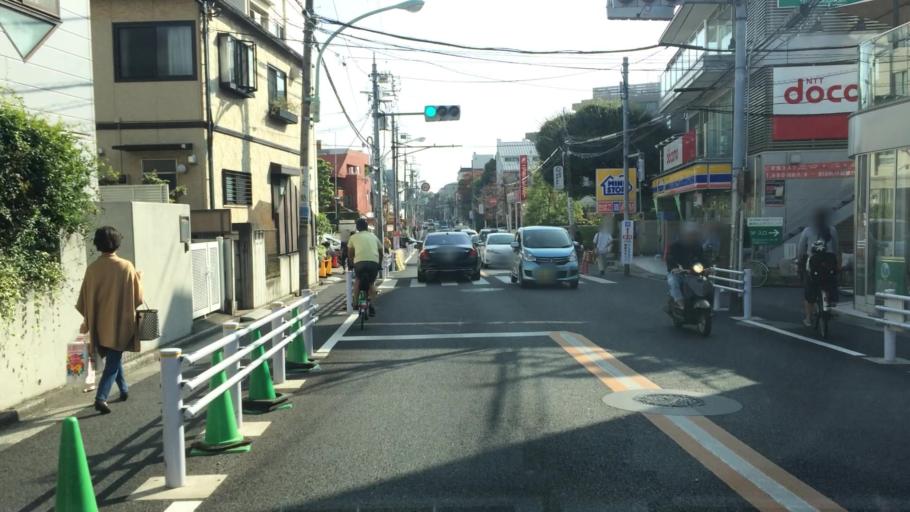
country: JP
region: Tokyo
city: Tokyo
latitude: 35.6319
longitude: 139.6617
